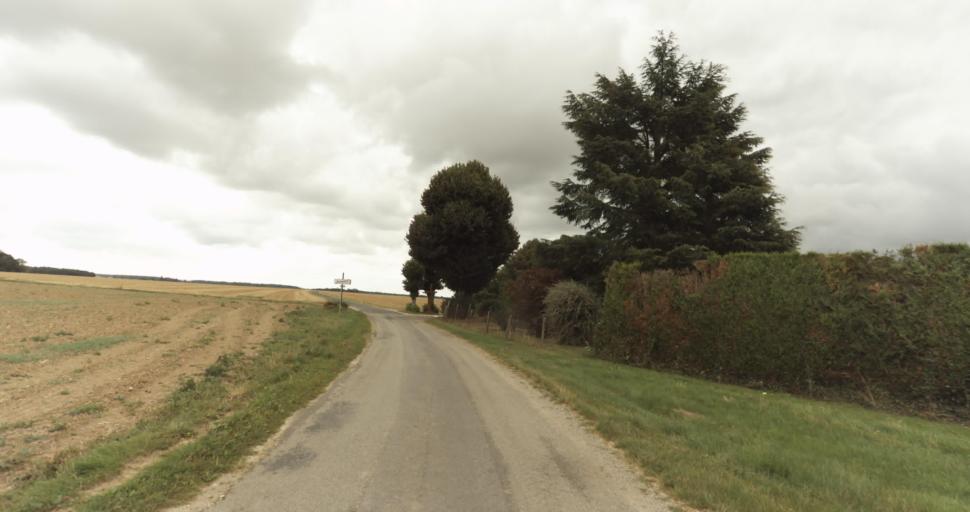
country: FR
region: Haute-Normandie
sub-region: Departement de l'Eure
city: Menilles
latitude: 49.0198
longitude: 1.2761
